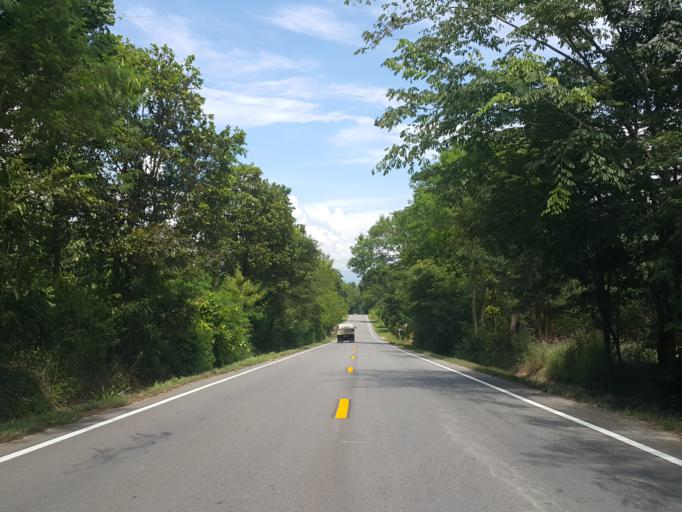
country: TH
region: Chiang Mai
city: Phrao
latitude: 19.2657
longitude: 99.1882
